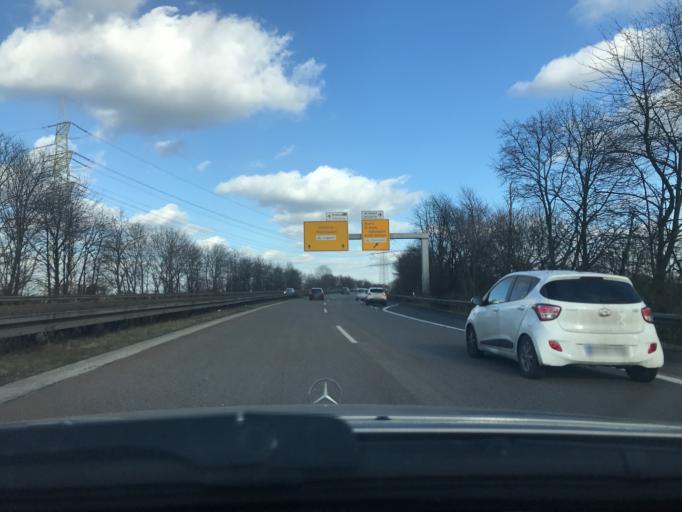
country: DE
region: North Rhine-Westphalia
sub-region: Regierungsbezirk Dusseldorf
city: Moers
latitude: 51.3815
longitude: 6.6462
